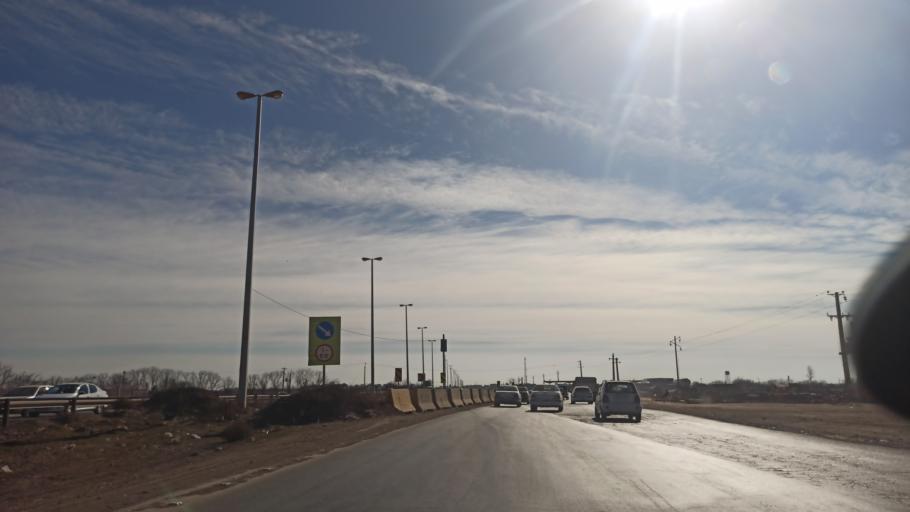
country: IR
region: Qazvin
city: Alvand
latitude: 36.1993
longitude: 50.0142
